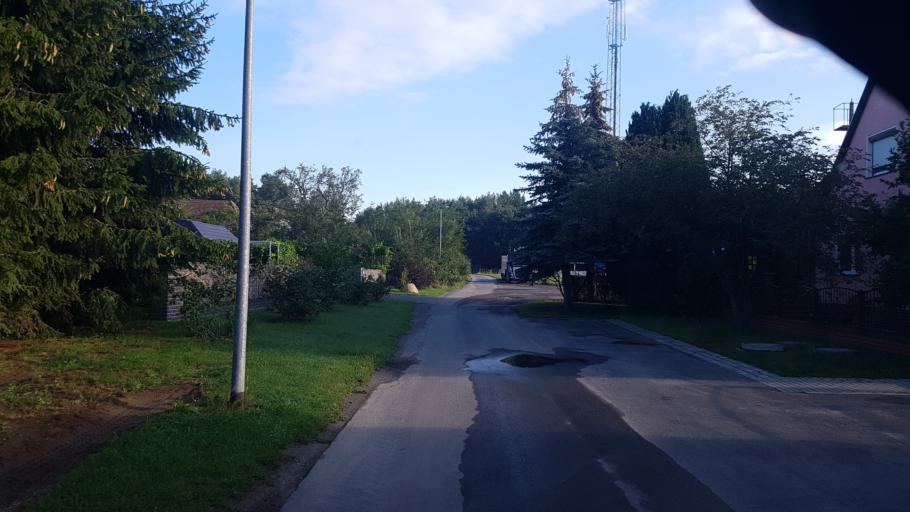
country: DE
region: Brandenburg
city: Bronkow
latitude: 51.6751
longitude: 13.8919
